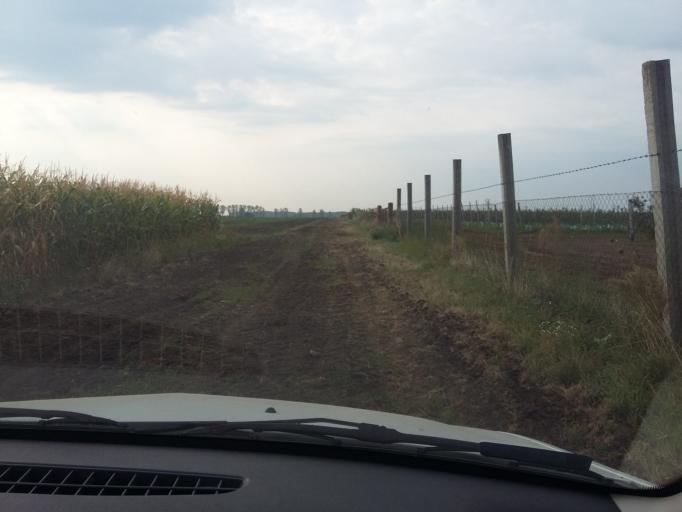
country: HU
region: Borsod-Abauj-Zemplen
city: Taktaharkany
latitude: 48.1285
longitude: 21.1071
